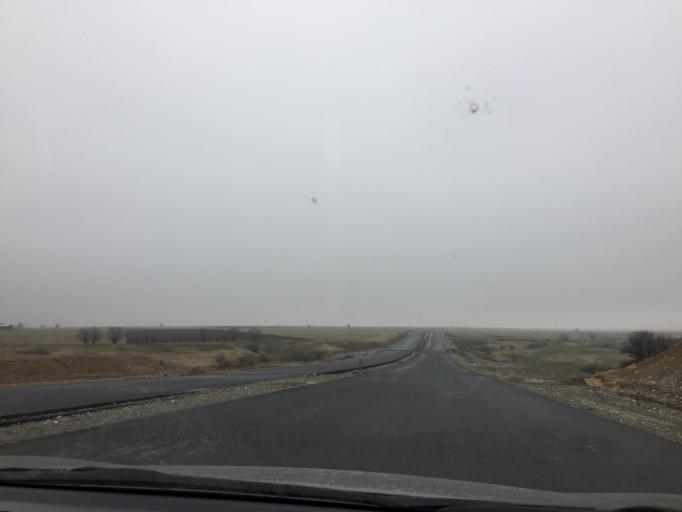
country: KZ
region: Ongtustik Qazaqstan
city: Turar Ryskulov
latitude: 42.5080
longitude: 70.4117
